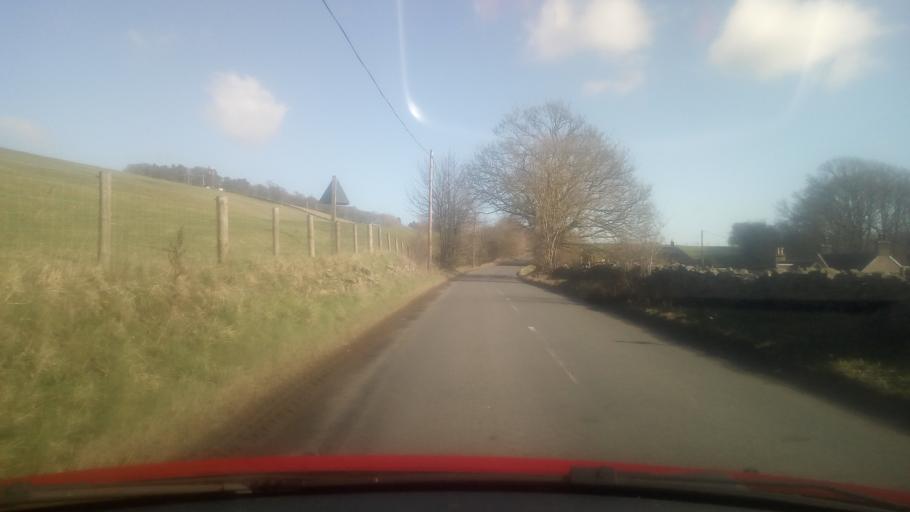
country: GB
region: Scotland
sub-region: The Scottish Borders
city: Selkirk
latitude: 55.5572
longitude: -2.8469
